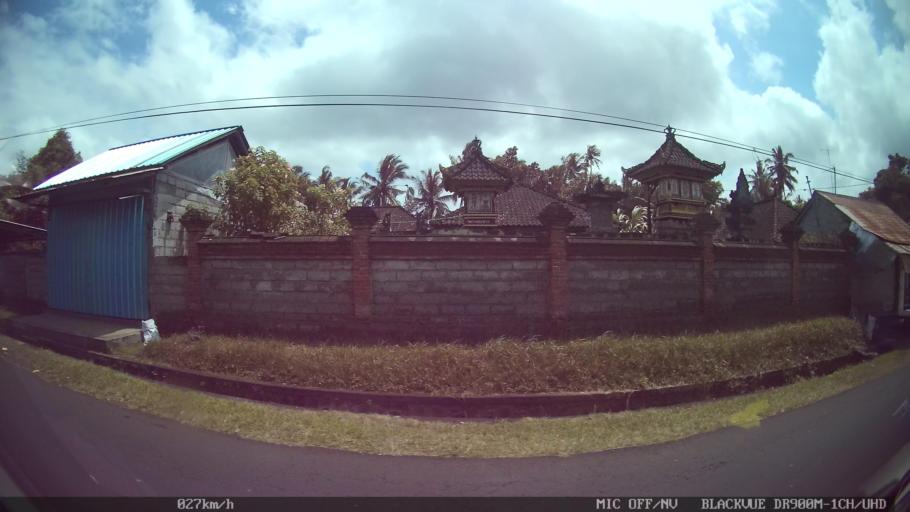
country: ID
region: Bali
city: Banjar Kelodan
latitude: -8.4862
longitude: 115.3677
